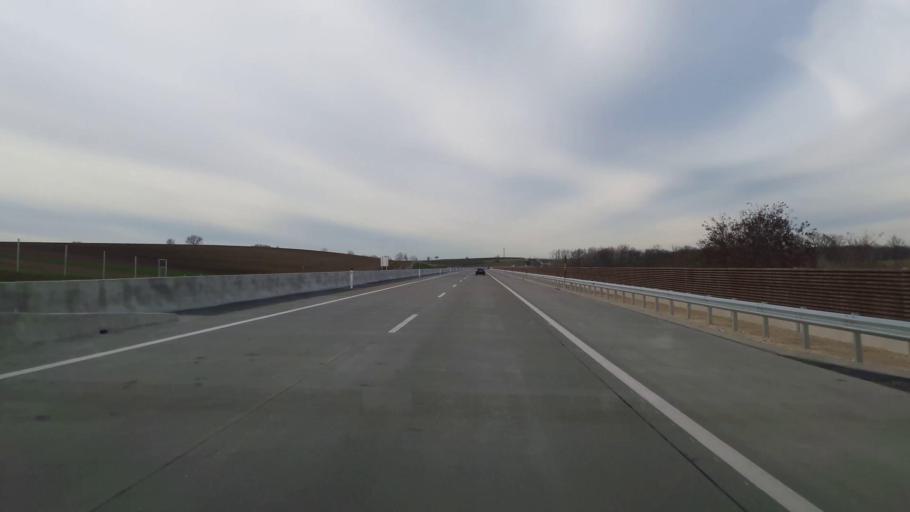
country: AT
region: Lower Austria
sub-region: Politischer Bezirk Mistelbach
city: Herrnbaumgarten
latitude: 48.6643
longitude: 16.6836
